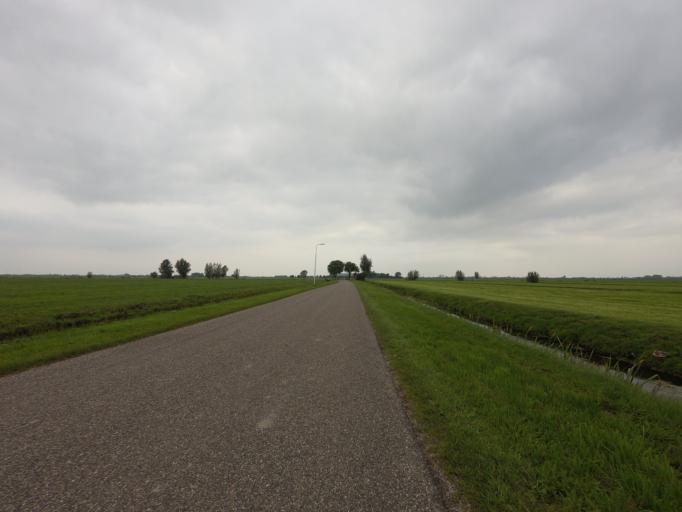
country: NL
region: South Holland
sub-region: Molenwaard
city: Liesveld
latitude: 51.8859
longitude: 4.7944
